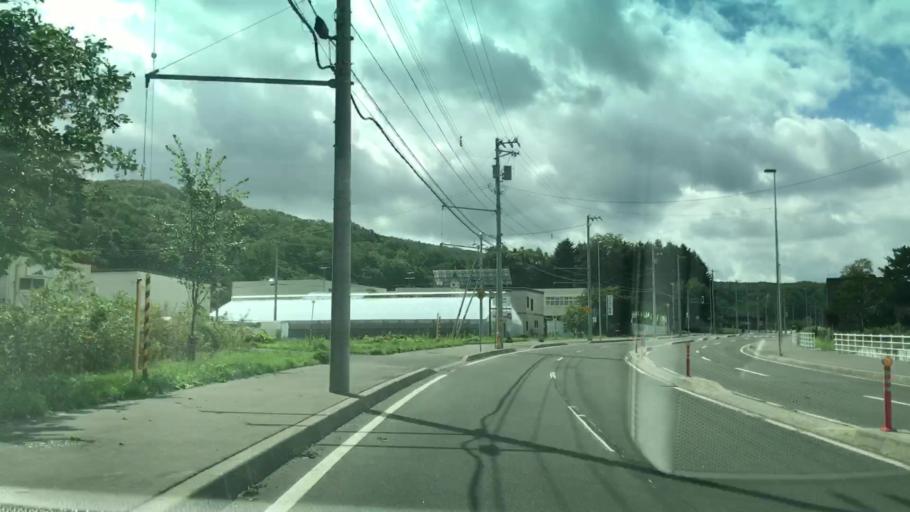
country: JP
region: Hokkaido
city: Kitahiroshima
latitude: 42.9518
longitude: 141.4513
